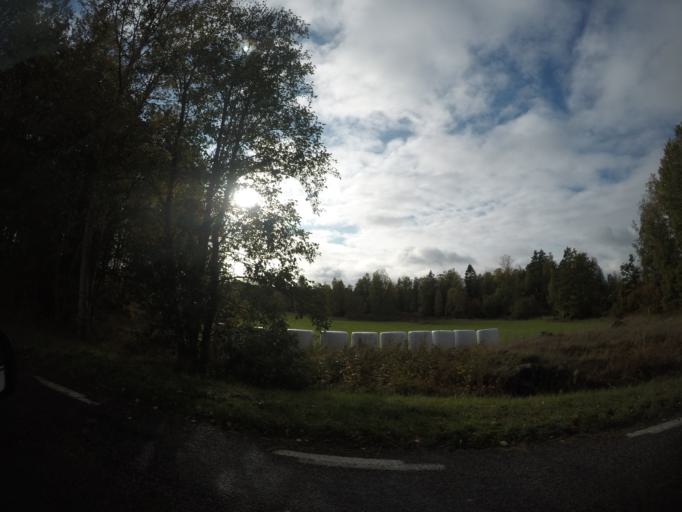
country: SE
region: Soedermanland
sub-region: Eskilstuna Kommun
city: Kvicksund
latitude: 59.3315
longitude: 16.2533
